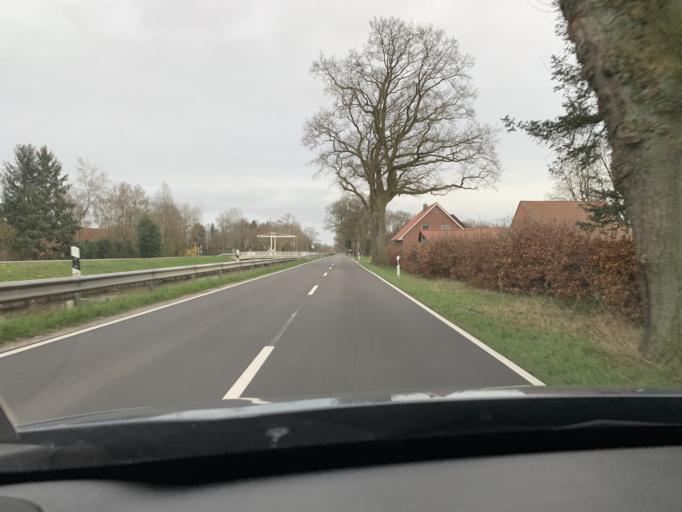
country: DE
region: Lower Saxony
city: Barssel
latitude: 53.1990
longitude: 7.7594
